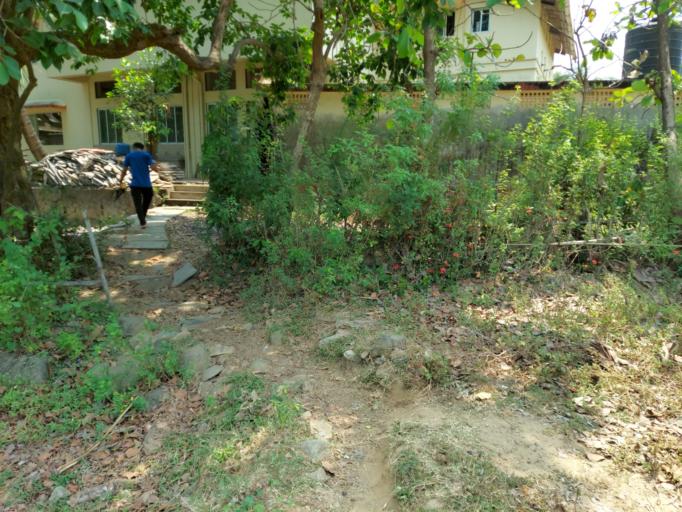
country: IN
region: Maharashtra
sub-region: Sindhudurg
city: Savantvadi
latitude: 15.9711
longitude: 73.7870
